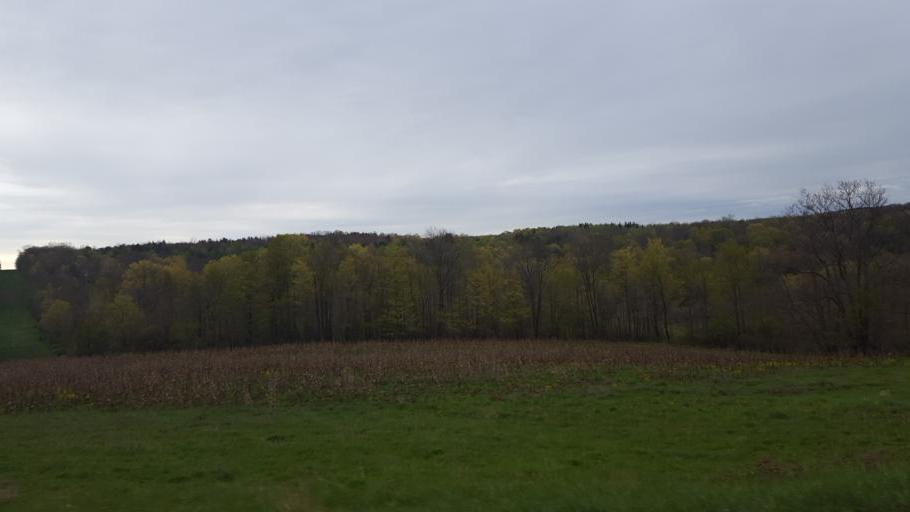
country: US
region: Pennsylvania
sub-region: Tioga County
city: Westfield
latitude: 42.0360
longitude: -77.4663
